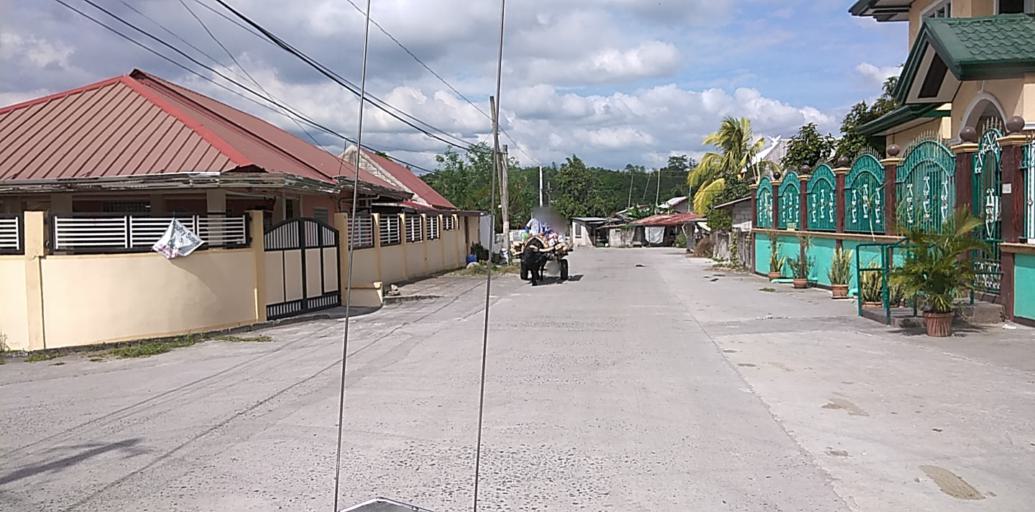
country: PH
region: Central Luzon
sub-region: Province of Pampanga
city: Porac
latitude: 15.0654
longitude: 120.5358
